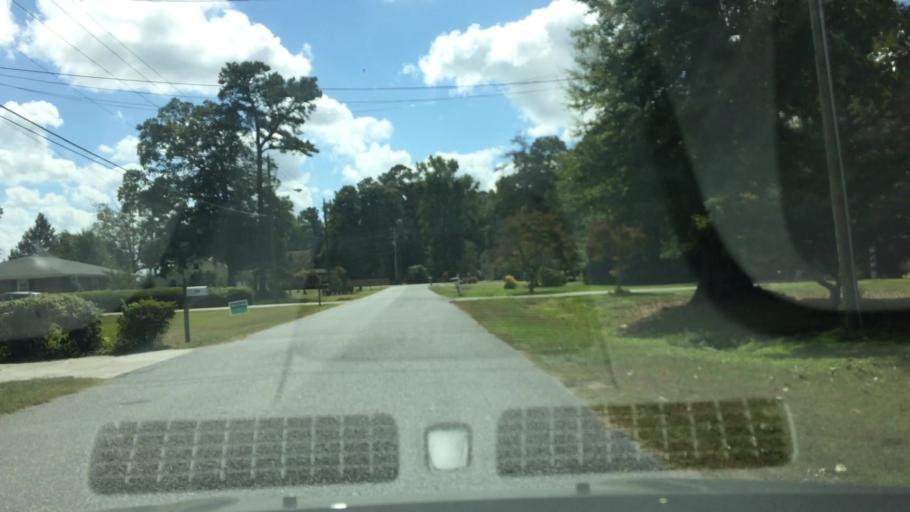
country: US
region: North Carolina
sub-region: Pitt County
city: Ayden
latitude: 35.4735
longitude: -77.4368
